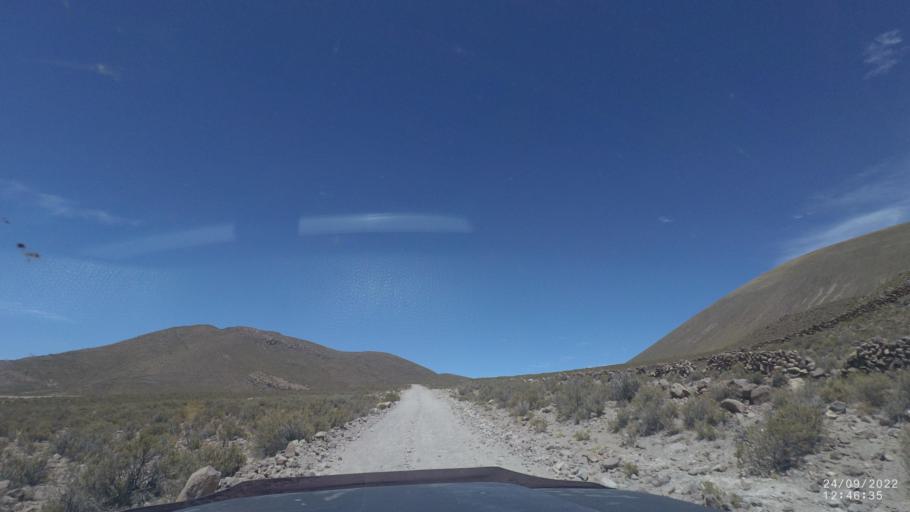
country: BO
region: Potosi
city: Colchani
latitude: -19.8042
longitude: -67.5710
